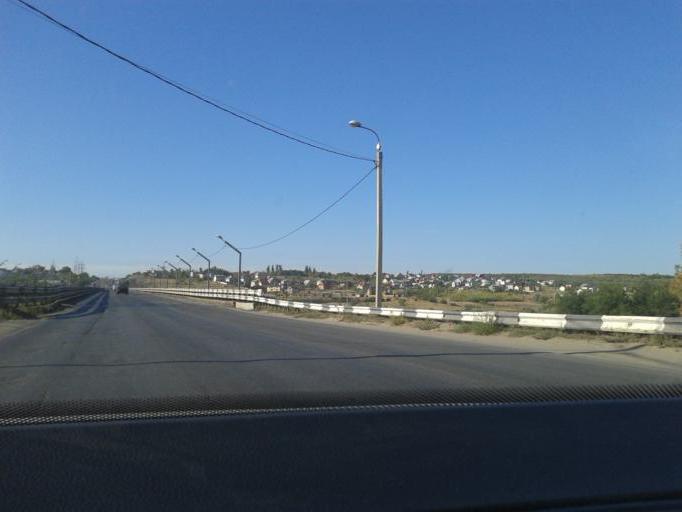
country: RU
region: Volgograd
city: Volgograd
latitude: 48.7187
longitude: 44.4449
